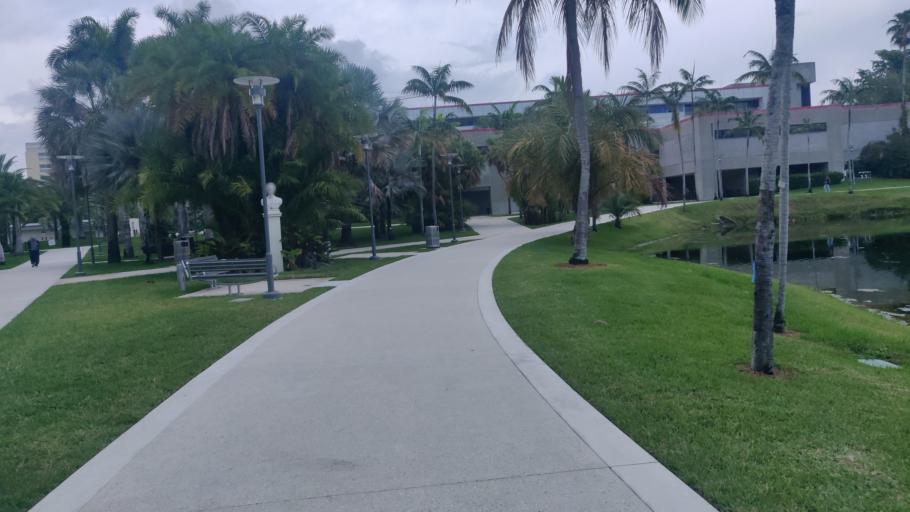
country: US
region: Florida
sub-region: Miami-Dade County
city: Sweetwater
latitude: 25.7580
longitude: -80.3740
